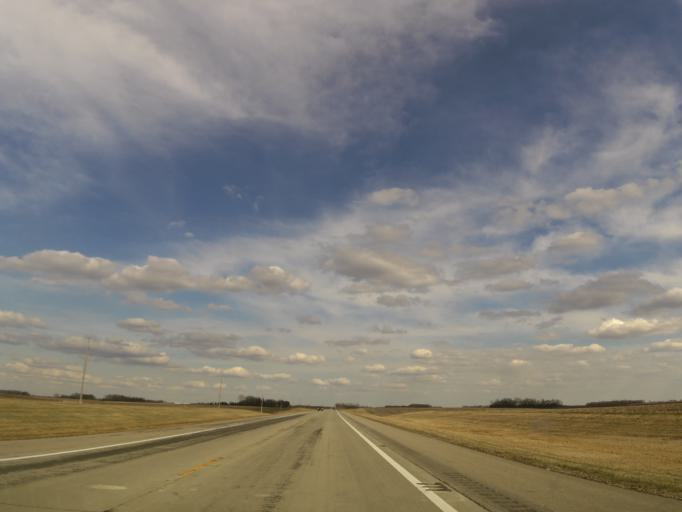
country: US
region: Minnesota
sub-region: Chippewa County
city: Montevideo
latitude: 44.9353
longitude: -95.8779
